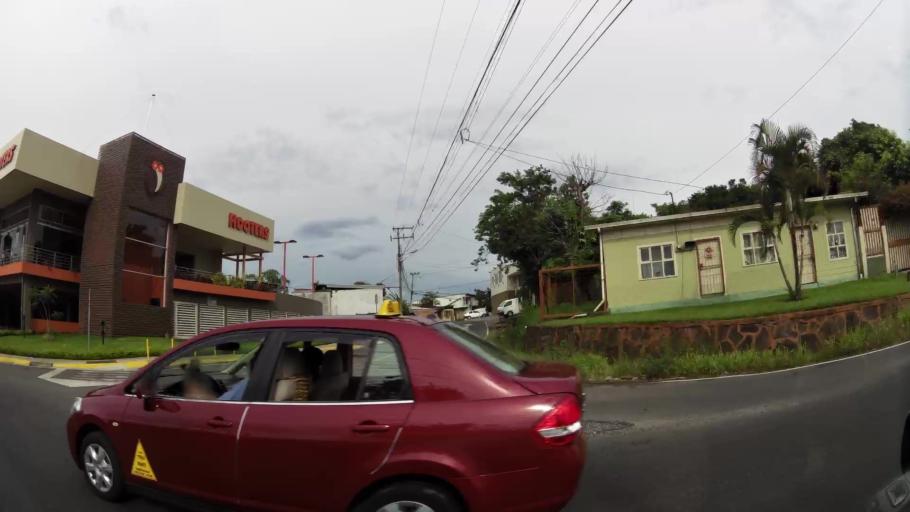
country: CR
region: San Jose
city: San Vicente de Moravia
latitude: 9.9627
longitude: -84.0616
